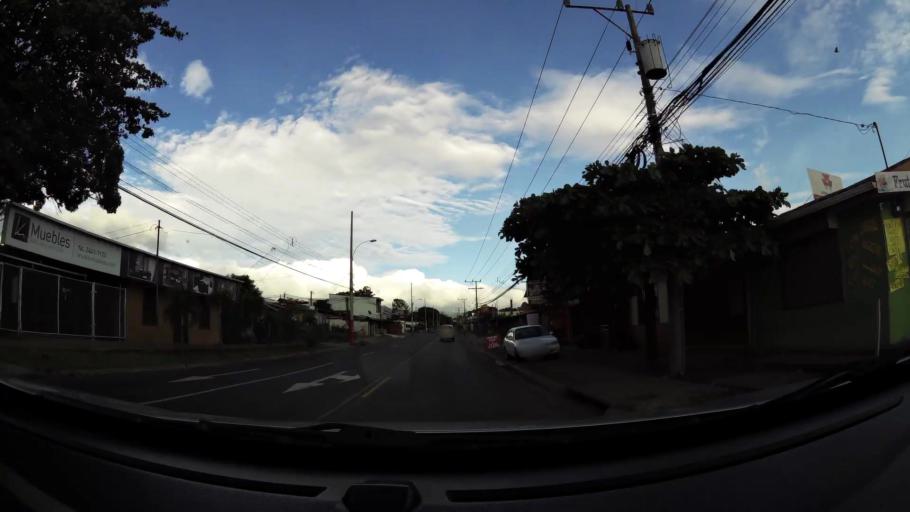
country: CR
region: Heredia
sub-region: Canton de Belen
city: San Antonio
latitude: 10.0035
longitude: -84.1857
